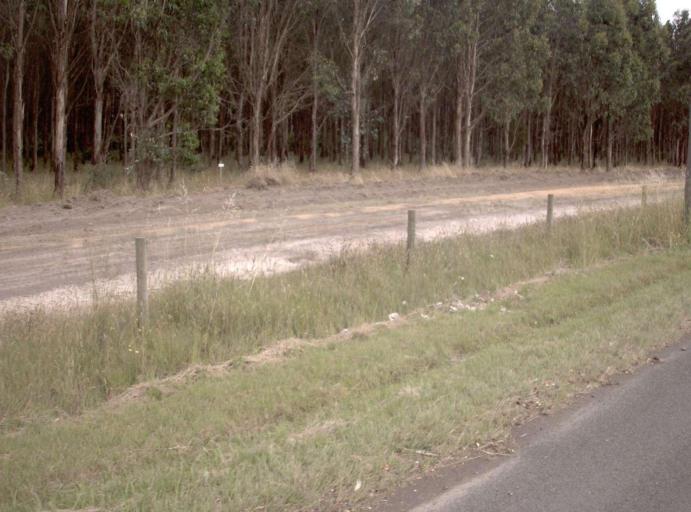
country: AU
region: Victoria
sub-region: Latrobe
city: Morwell
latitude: -38.2085
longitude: 146.4461
